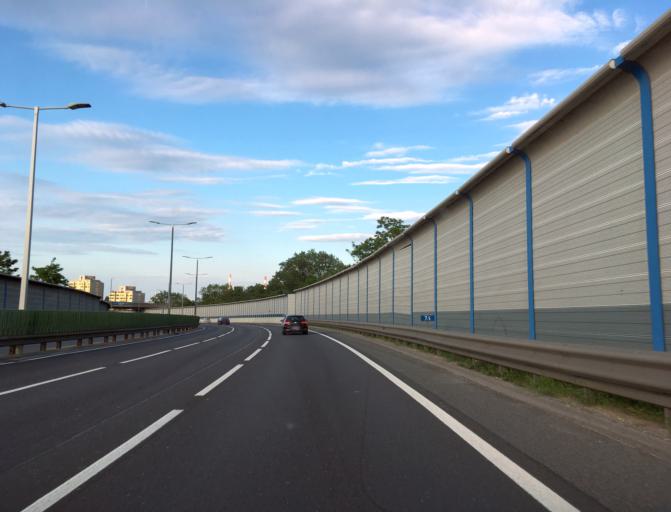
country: AT
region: Vienna
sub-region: Wien Stadt
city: Vienna
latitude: 48.1702
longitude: 16.3962
